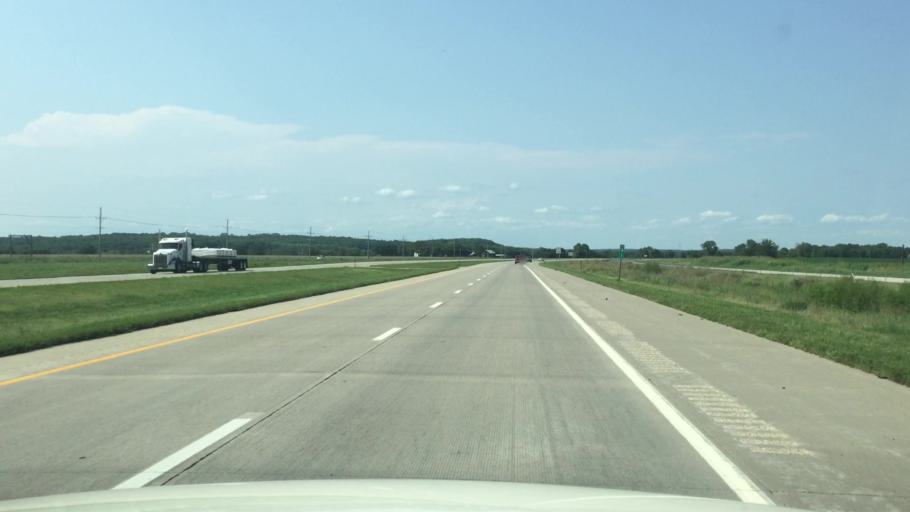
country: US
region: Kansas
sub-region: Linn County
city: Pleasanton
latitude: 38.1884
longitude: -94.7031
